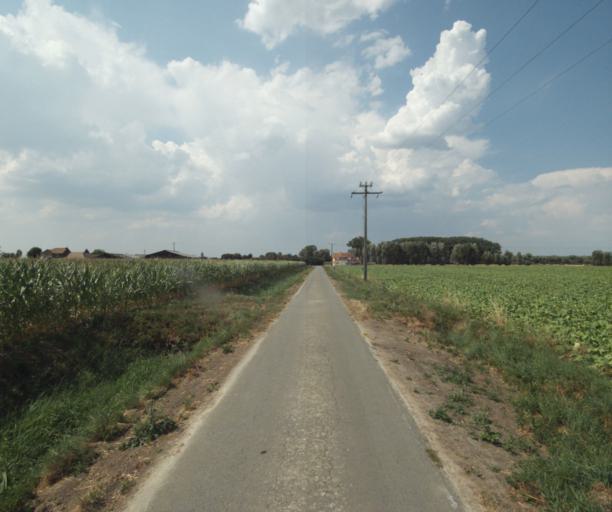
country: FR
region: Nord-Pas-de-Calais
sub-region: Departement du Nord
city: Deulemont
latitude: 50.7433
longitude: 2.9738
